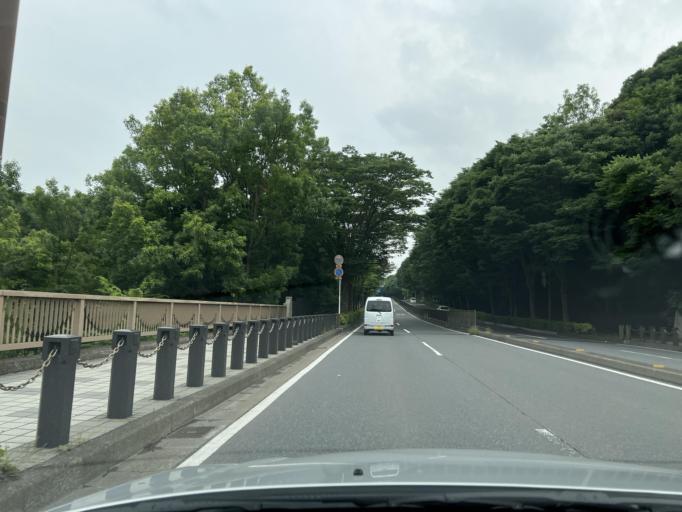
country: JP
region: Chiba
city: Matsudo
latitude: 35.8026
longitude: 139.9403
